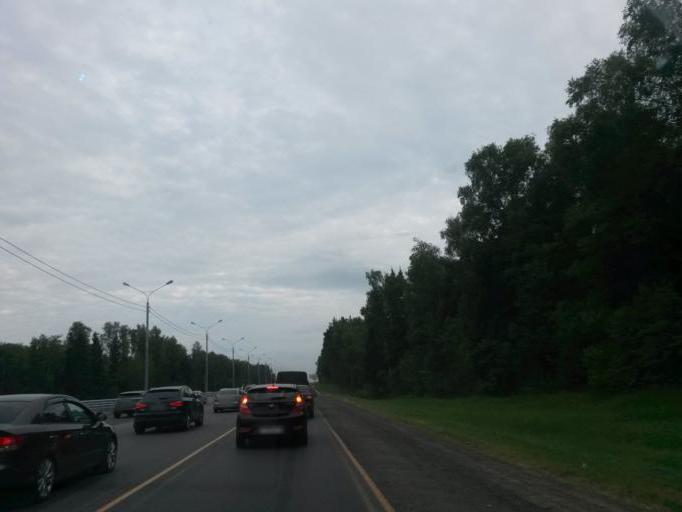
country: RU
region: Moskovskaya
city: Lyubuchany
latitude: 55.2664
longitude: 37.5356
